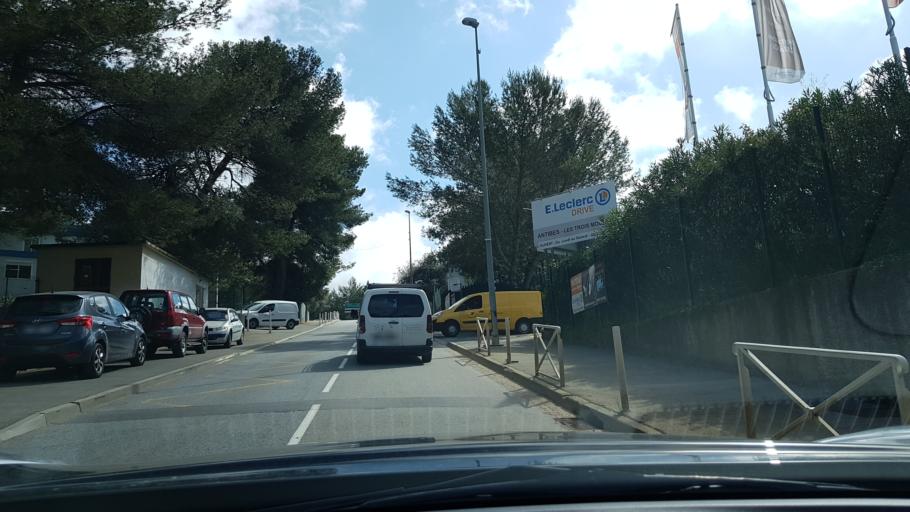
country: FR
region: Provence-Alpes-Cote d'Azur
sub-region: Departement des Alpes-Maritimes
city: Biot
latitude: 43.6041
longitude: 7.0772
